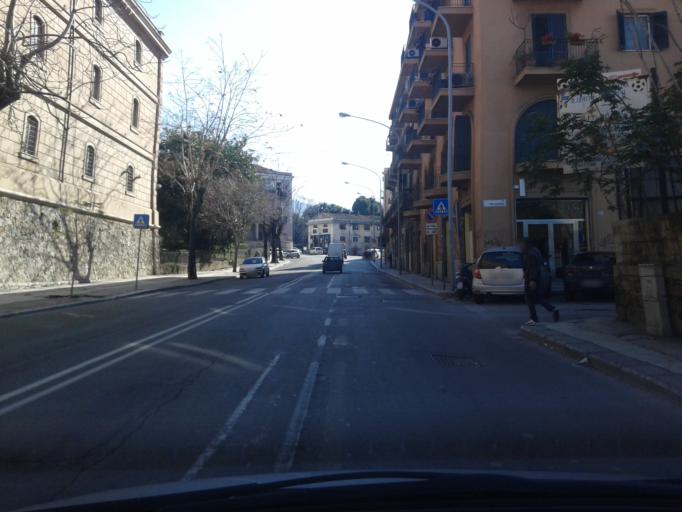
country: IT
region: Sicily
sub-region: Palermo
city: Palermo
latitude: 38.1133
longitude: 13.3523
